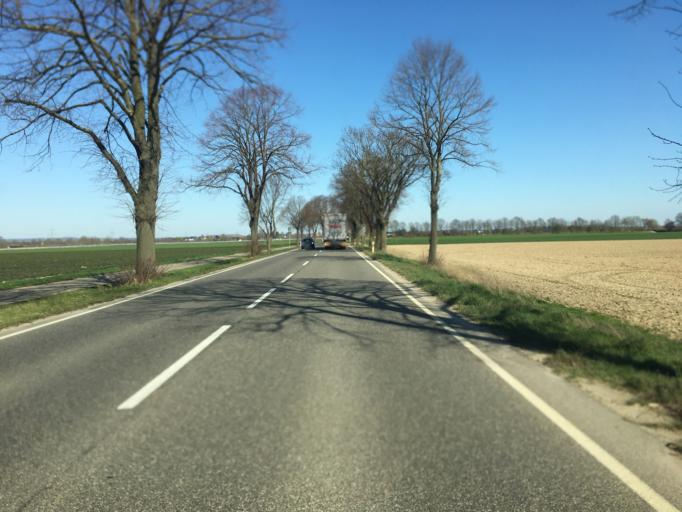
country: DE
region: North Rhine-Westphalia
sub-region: Regierungsbezirk Koln
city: Norvenich
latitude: 50.8447
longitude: 6.6055
